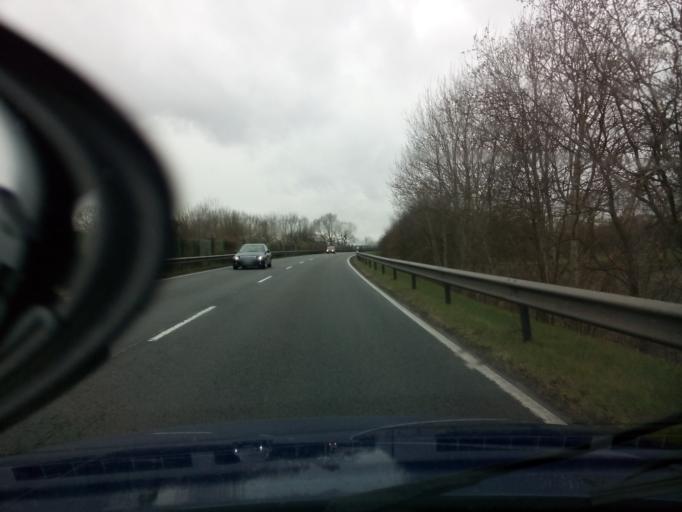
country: DE
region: Lower Saxony
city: Haselunne
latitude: 52.6833
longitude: 7.4570
